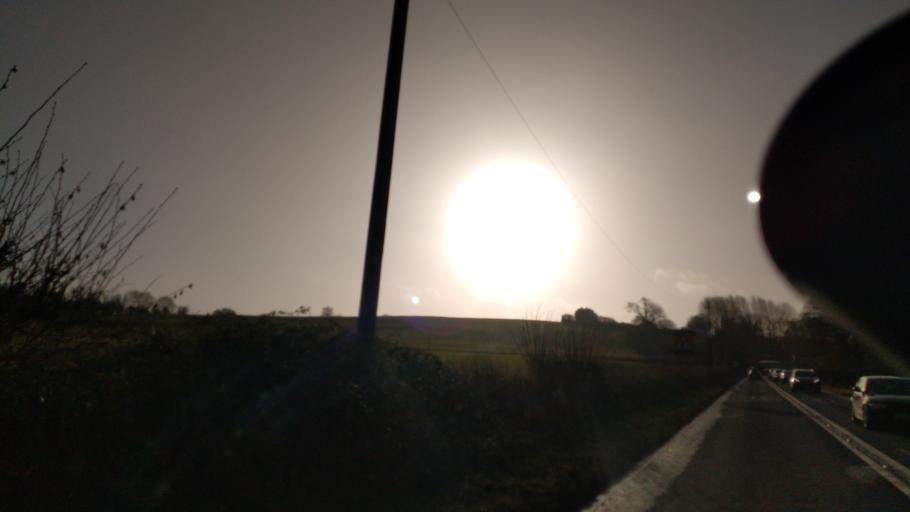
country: GB
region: England
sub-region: Somerset
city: Evercreech
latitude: 51.1431
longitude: -2.5482
